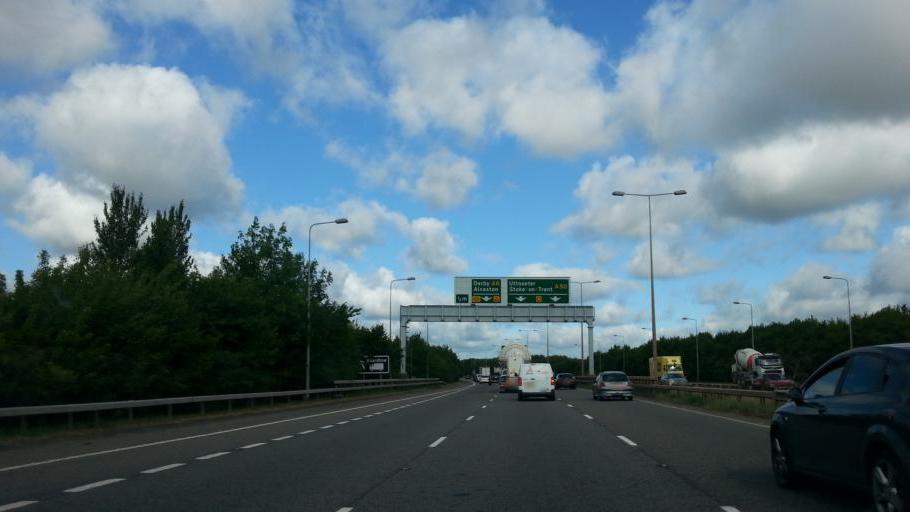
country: GB
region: England
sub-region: Leicestershire
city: Castle Donington
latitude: 52.8686
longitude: -1.3705
